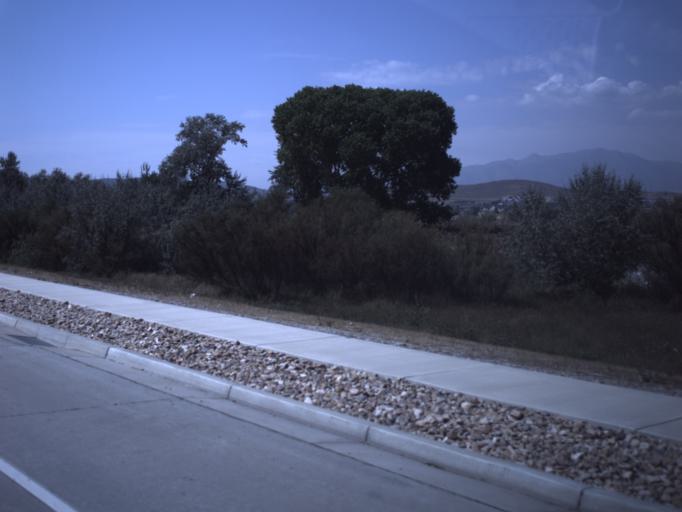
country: US
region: Utah
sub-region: Utah County
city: Saratoga Springs
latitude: 40.3738
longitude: -111.9048
